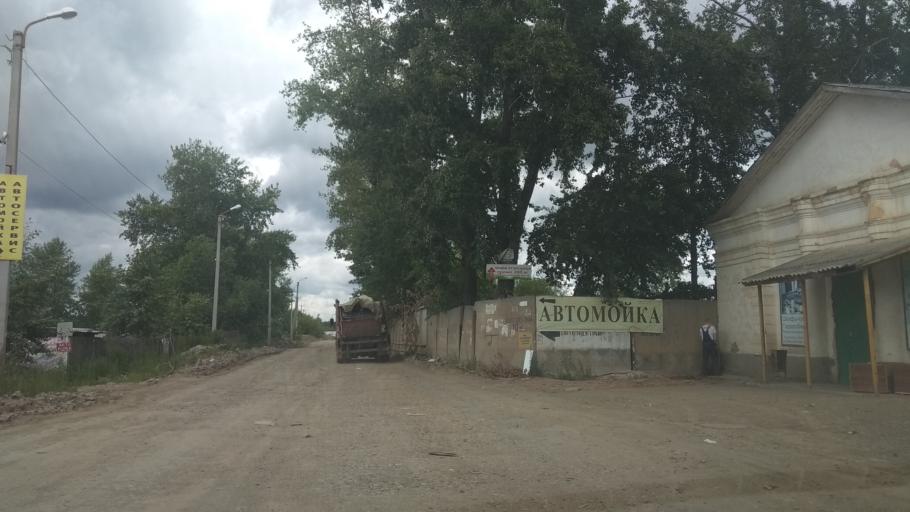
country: RU
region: Sverdlovsk
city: Verkhnyaya Pyshma
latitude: 56.9159
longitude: 60.5762
